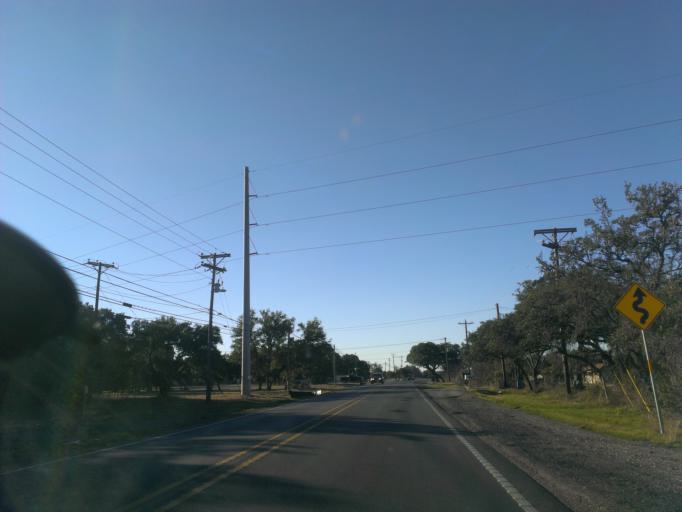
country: US
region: Texas
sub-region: Hays County
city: Dripping Springs
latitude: 30.1748
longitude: -98.0854
